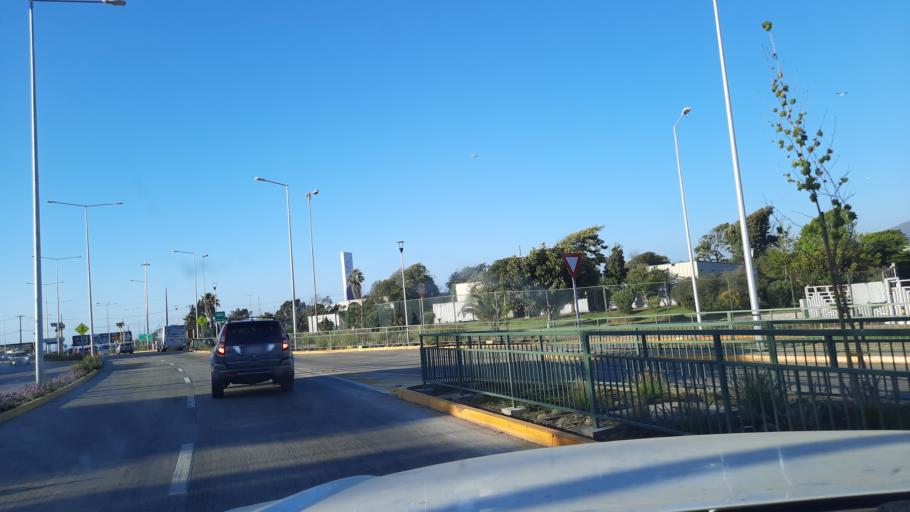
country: CL
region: Valparaiso
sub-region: Provincia de Valparaiso
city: Vina del Mar
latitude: -32.9236
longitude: -71.5065
